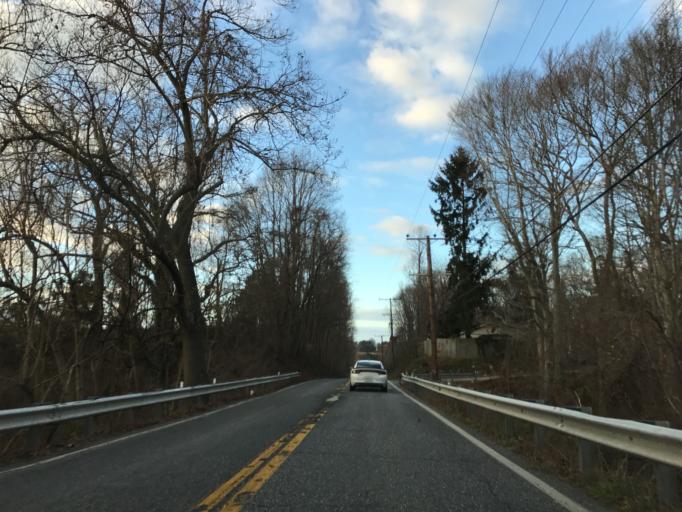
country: US
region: Maryland
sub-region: Harford County
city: Aberdeen
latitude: 39.5897
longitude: -76.1852
